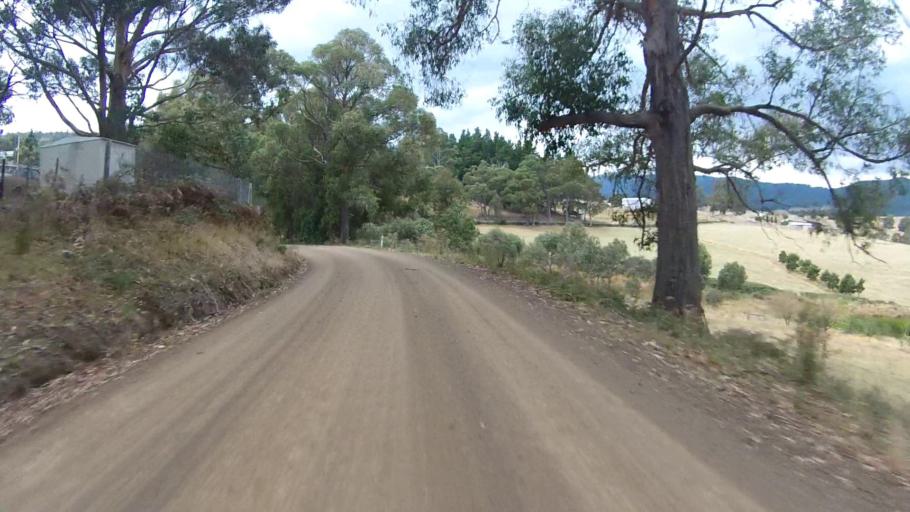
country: AU
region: Tasmania
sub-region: Huon Valley
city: Huonville
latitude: -42.9711
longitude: 147.0603
